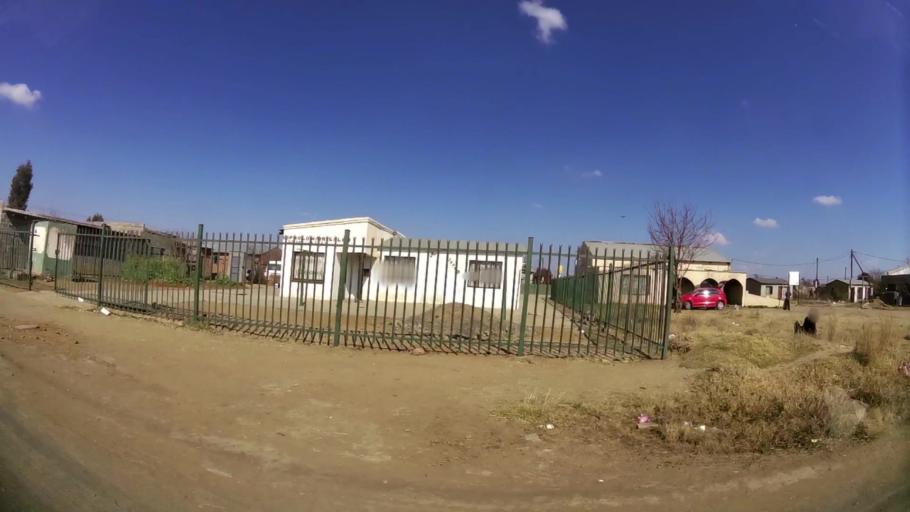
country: ZA
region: Orange Free State
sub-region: Mangaung Metropolitan Municipality
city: Bloemfontein
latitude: -29.1472
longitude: 26.2795
